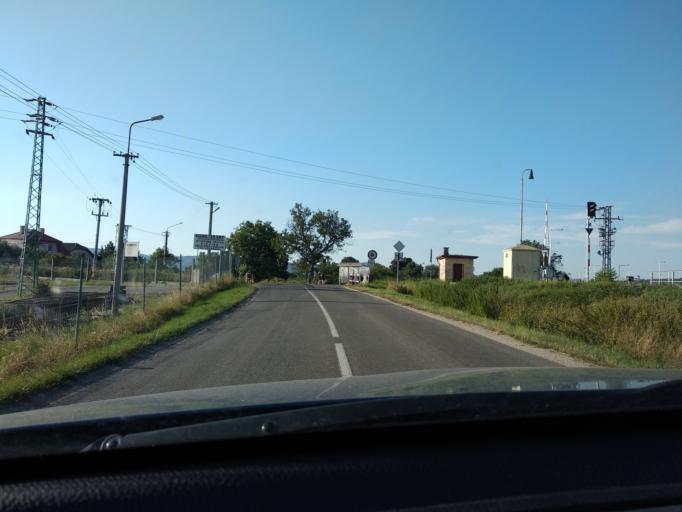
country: SK
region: Trenciansky
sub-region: Okres Trencin
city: Trencin
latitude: 48.8622
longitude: 18.0179
